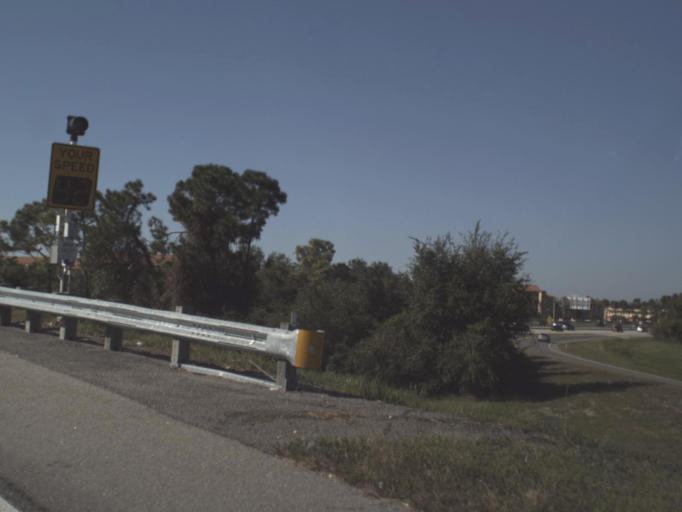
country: US
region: Florida
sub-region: Orange County
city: Williamsburg
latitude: 28.4220
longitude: -81.4729
